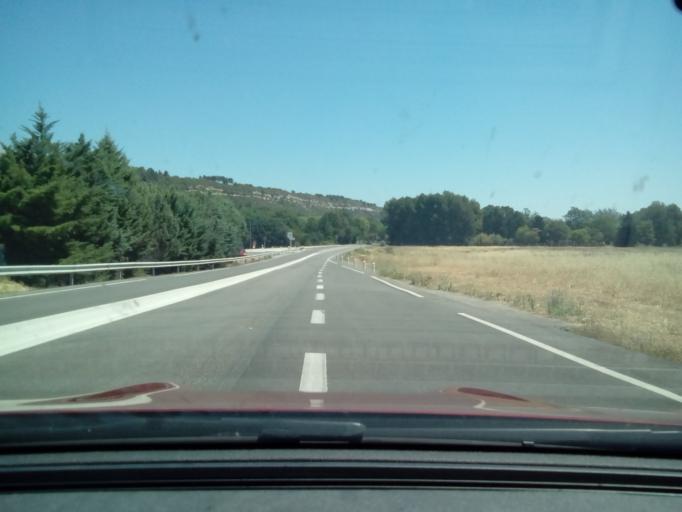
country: FR
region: Provence-Alpes-Cote d'Azur
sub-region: Departement des Bouches-du-Rhone
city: Chateauneuf-le-Rouge
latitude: 43.4782
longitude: 5.5415
